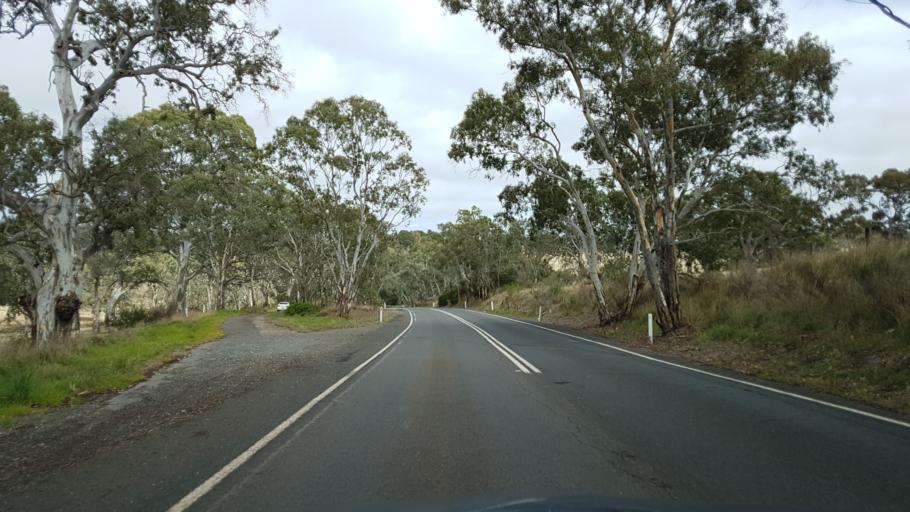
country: AU
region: South Australia
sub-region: Mount Barker
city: Nairne
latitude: -35.0414
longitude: 138.9337
